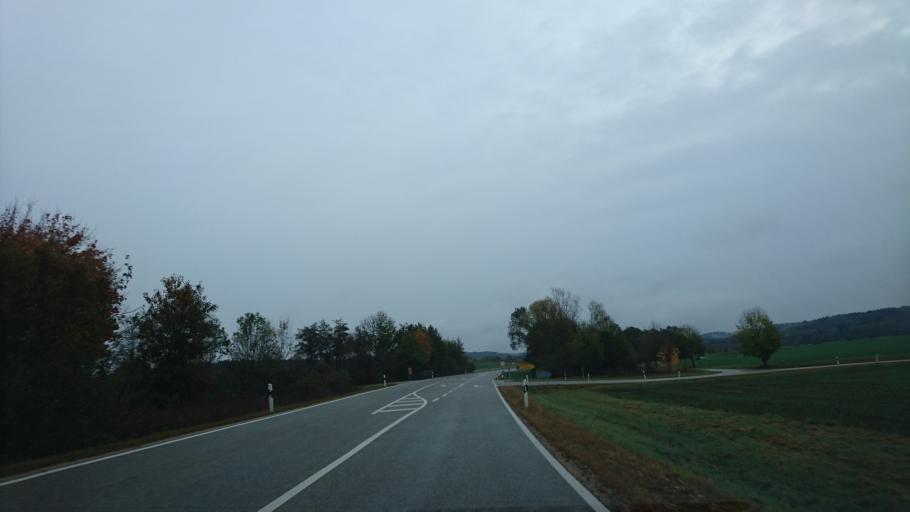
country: DE
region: Bavaria
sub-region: Regierungsbezirk Mittelfranken
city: Ettenstatt
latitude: 49.0845
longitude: 11.0639
